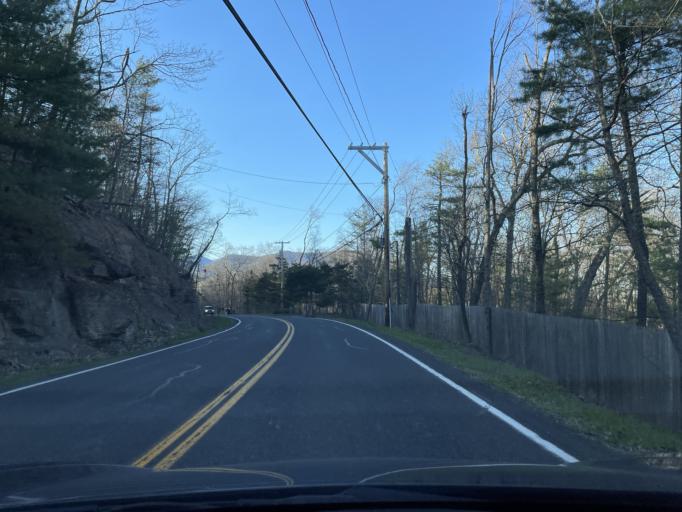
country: US
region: New York
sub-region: Ulster County
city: West Hurley
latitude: 42.0084
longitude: -74.1163
